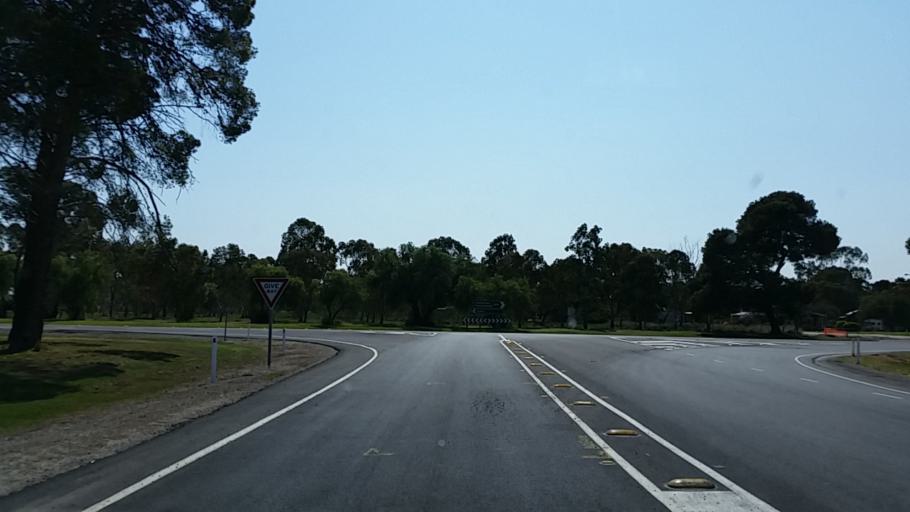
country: AU
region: South Australia
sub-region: Northern Areas
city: Jamestown
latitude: -33.1812
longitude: 138.4791
